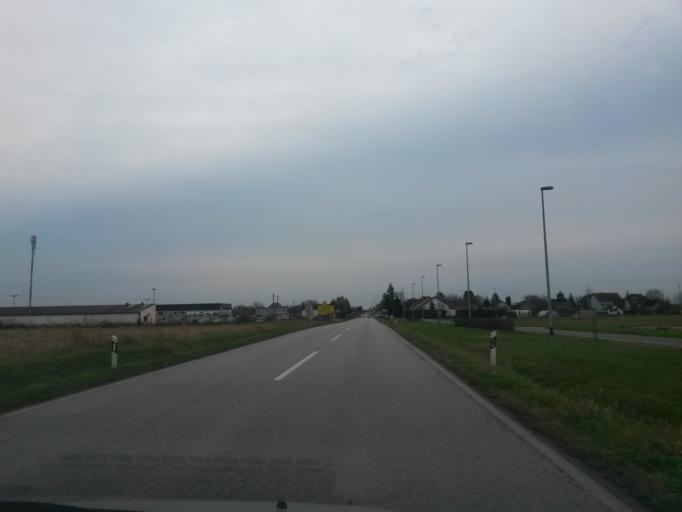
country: HR
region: Osjecko-Baranjska
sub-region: Grad Osijek
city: Bilje
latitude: 45.6133
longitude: 18.7337
